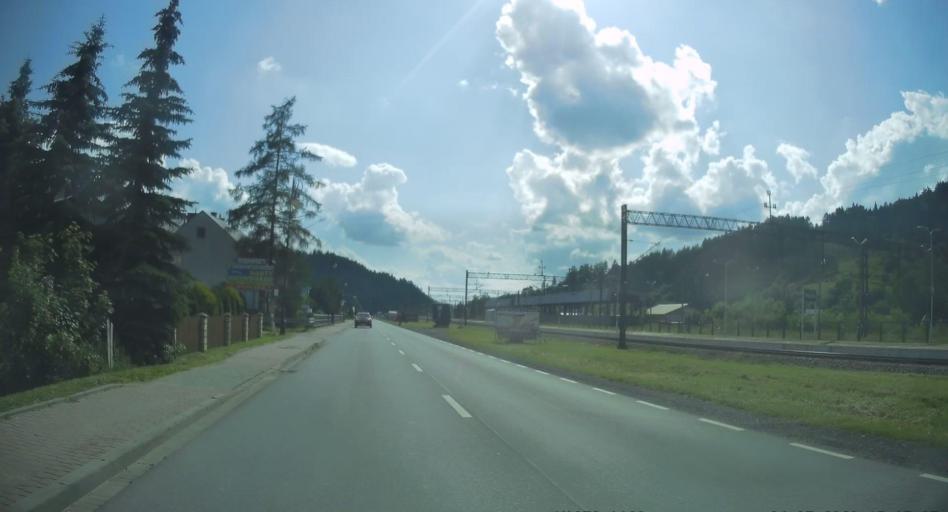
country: PL
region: Lesser Poland Voivodeship
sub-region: Powiat nowosadecki
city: Muszyna
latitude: 49.3684
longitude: 20.9416
